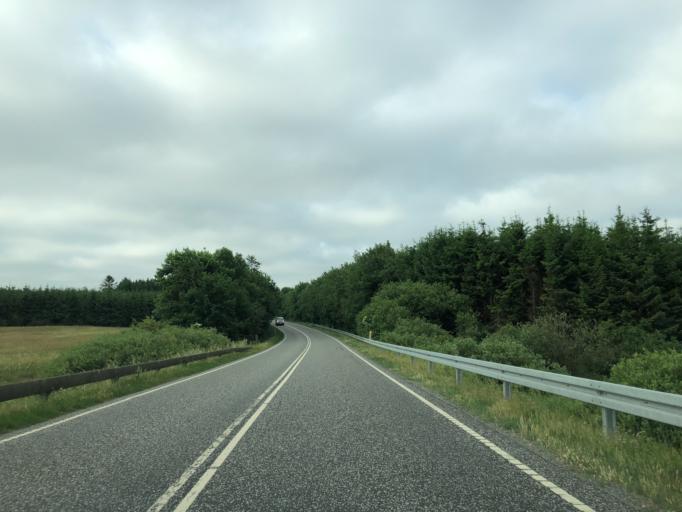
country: DK
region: South Denmark
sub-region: Vejle Kommune
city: Give
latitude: 55.7881
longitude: 9.2735
